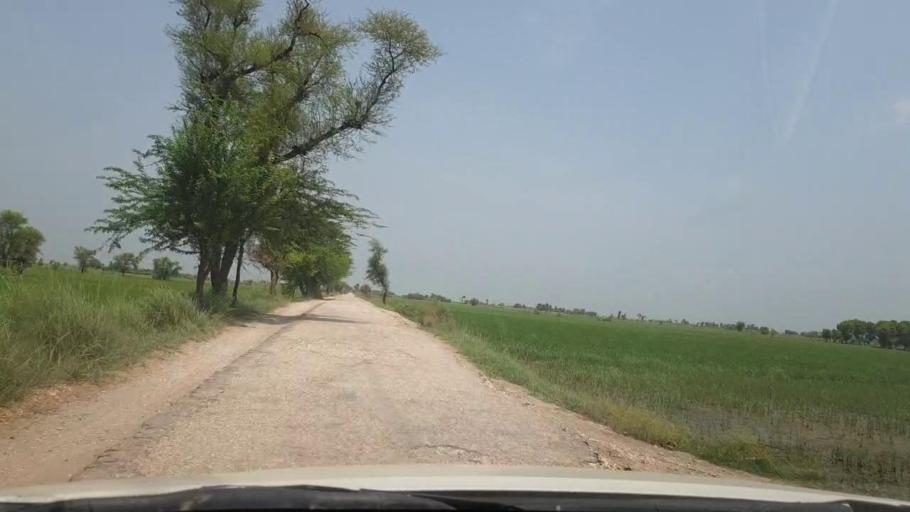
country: PK
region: Sindh
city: Rustam jo Goth
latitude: 28.0351
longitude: 68.8140
